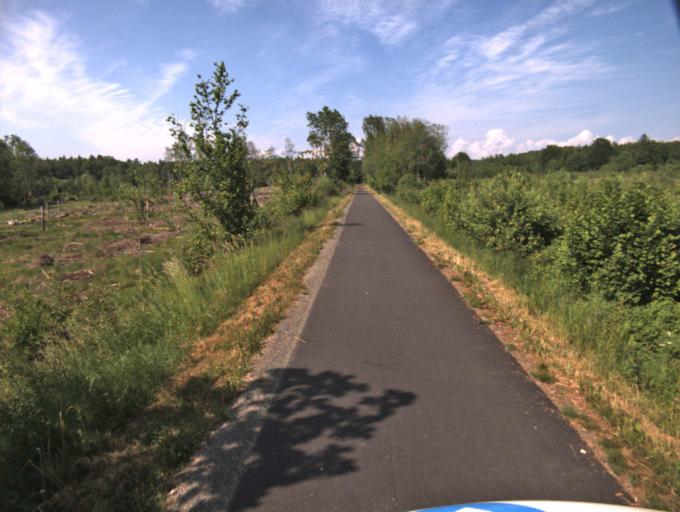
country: SE
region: Skane
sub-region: Kristianstads Kommun
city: Tollarp
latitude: 56.1938
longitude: 14.2889
